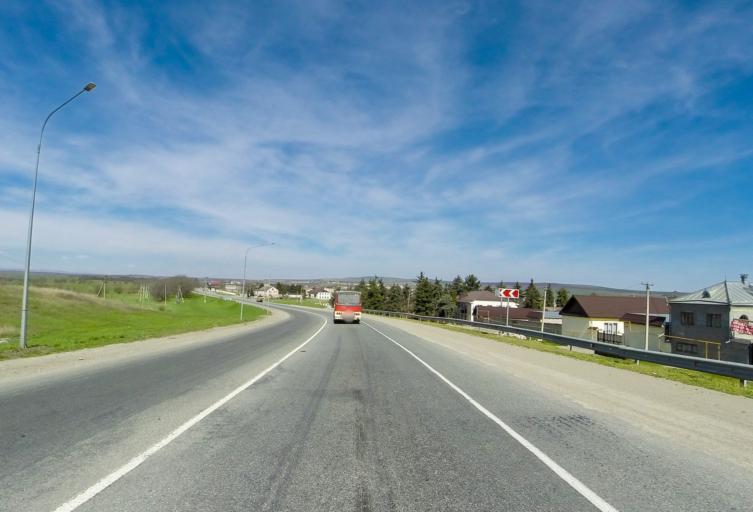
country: RU
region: Kabardino-Balkariya
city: Kuba-Taba
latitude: 43.7685
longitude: 43.4618
